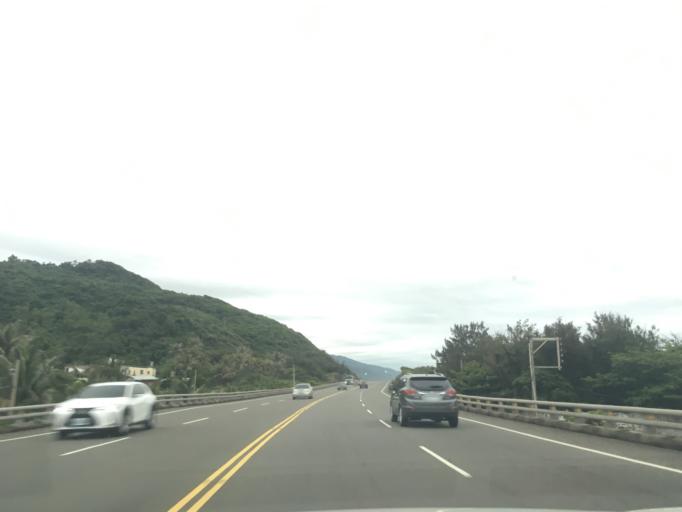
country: TW
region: Taiwan
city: Hengchun
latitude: 22.3075
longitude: 120.8900
